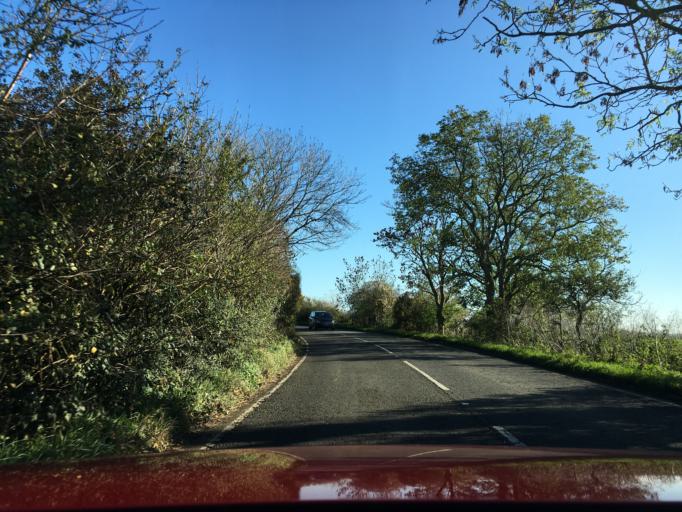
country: GB
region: England
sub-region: Somerset
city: Langport
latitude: 51.0339
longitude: -2.7926
